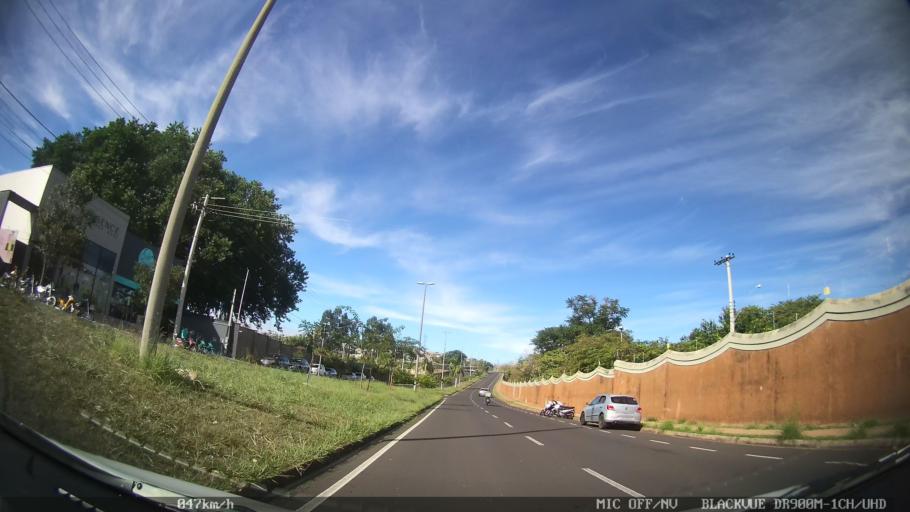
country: BR
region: Sao Paulo
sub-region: Sao Jose Do Rio Preto
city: Sao Jose do Rio Preto
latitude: -20.8086
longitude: -49.3446
